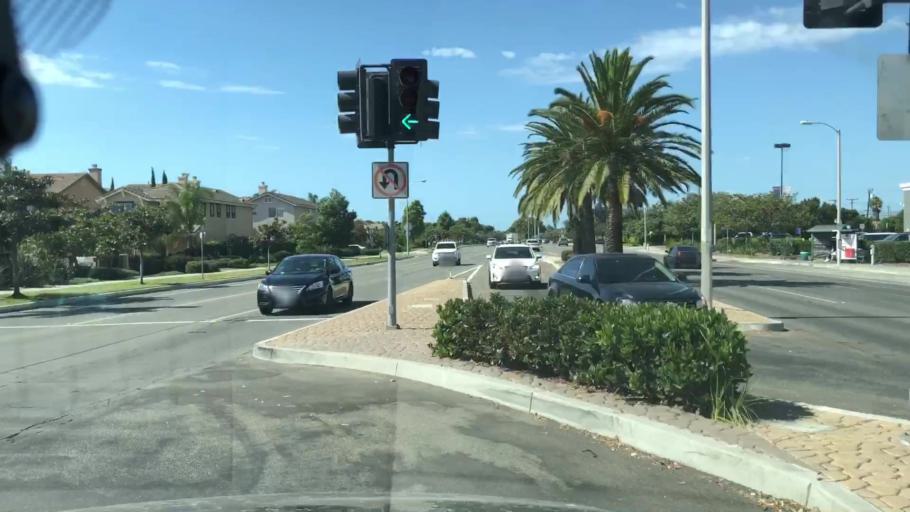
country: US
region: California
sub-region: Ventura County
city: El Rio
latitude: 34.2189
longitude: -119.1607
